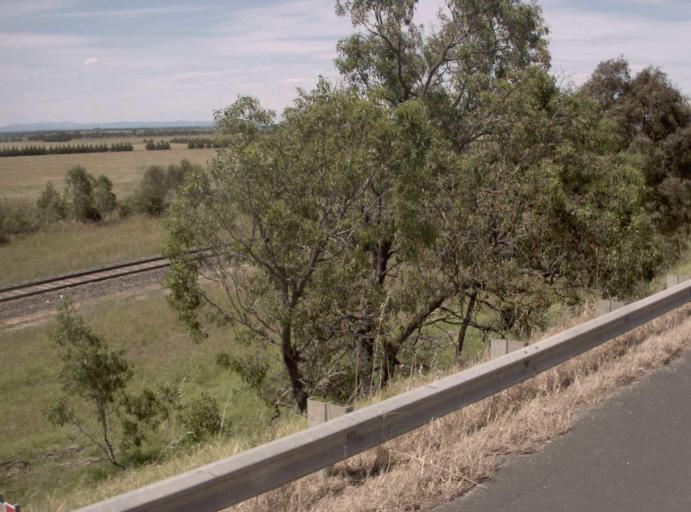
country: AU
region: Victoria
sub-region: Wellington
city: Sale
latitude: -38.1059
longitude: 146.9065
